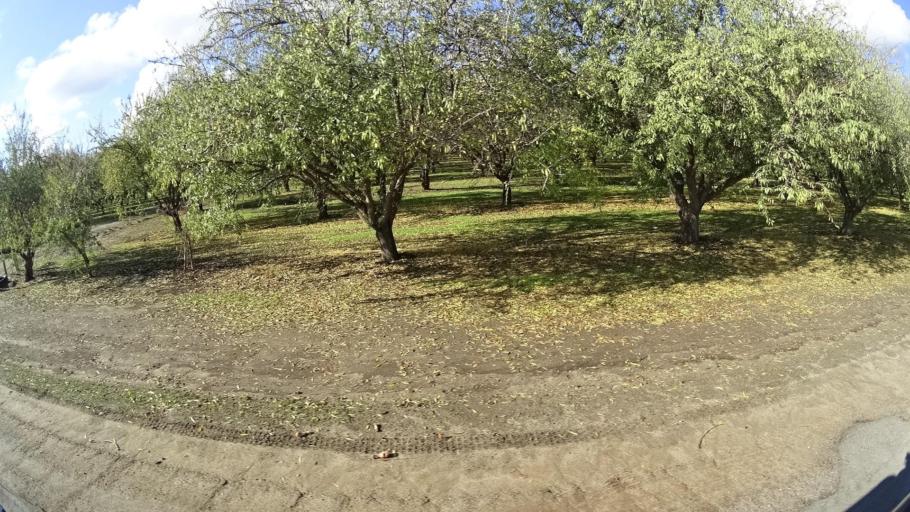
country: US
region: California
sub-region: Kern County
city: McFarland
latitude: 35.6493
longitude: -119.2322
